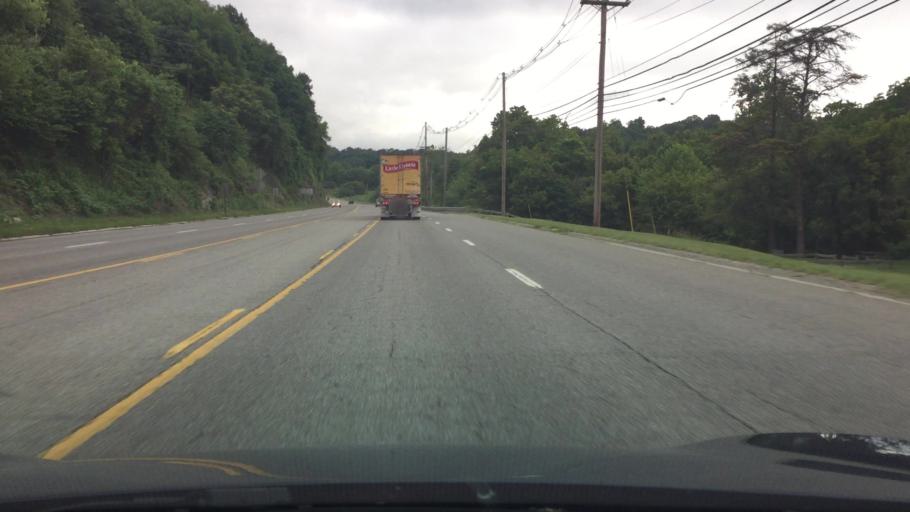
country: US
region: Virginia
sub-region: Montgomery County
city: Shawsville
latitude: 37.2476
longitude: -80.1755
